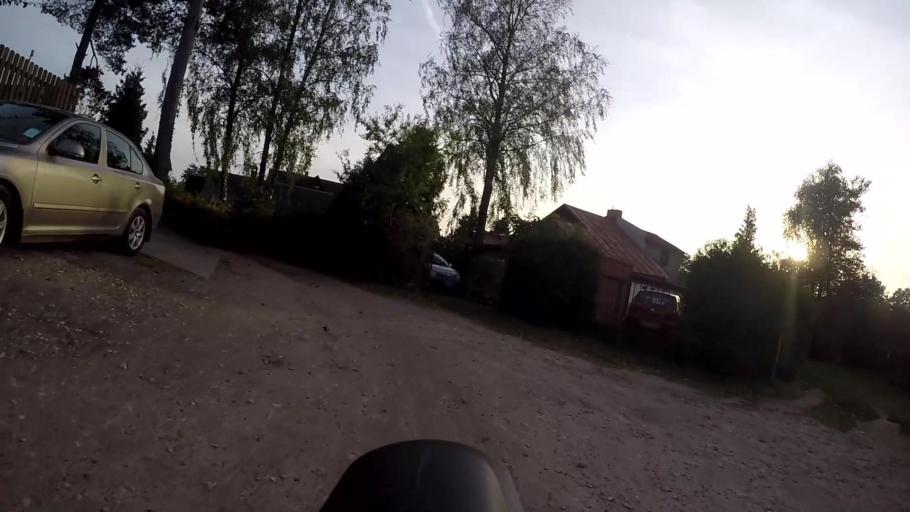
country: LV
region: Saulkrastu
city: Saulkrasti
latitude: 57.1897
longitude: 24.3532
